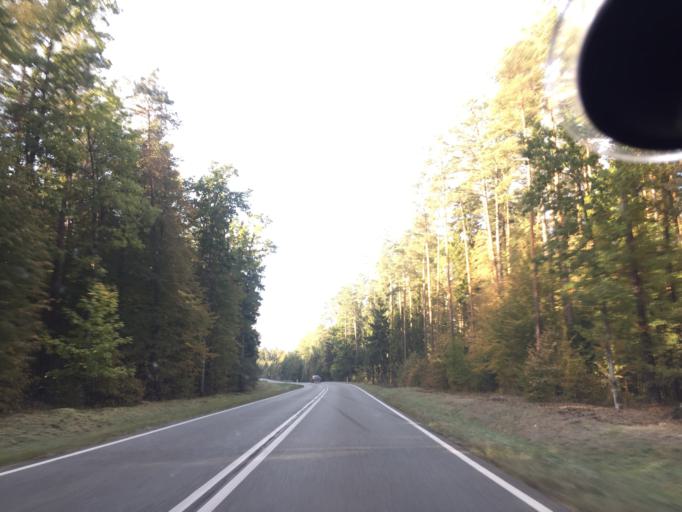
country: PL
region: Warmian-Masurian Voivodeship
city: Dobre Miasto
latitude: 54.0647
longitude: 20.4593
